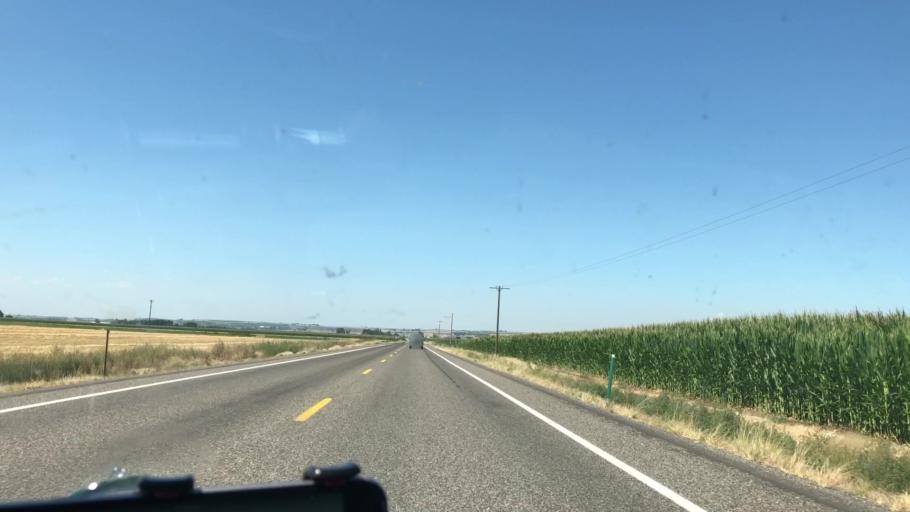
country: US
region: Idaho
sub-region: Owyhee County
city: Marsing
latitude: 43.5285
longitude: -116.8515
